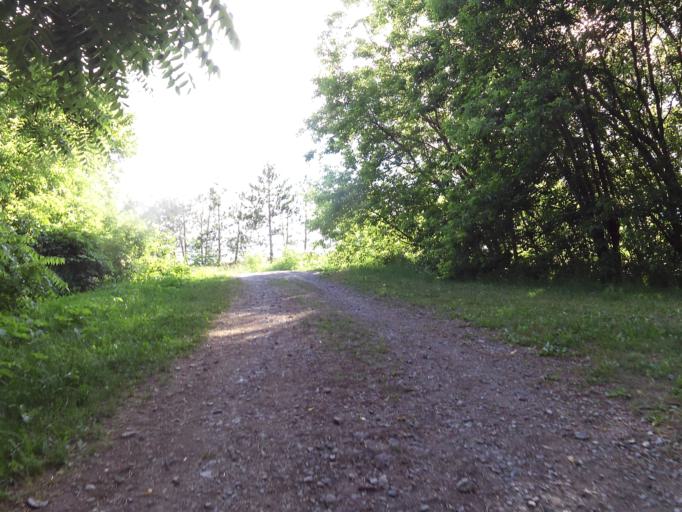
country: CA
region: Ontario
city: Arnprior
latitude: 45.3309
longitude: -76.2925
